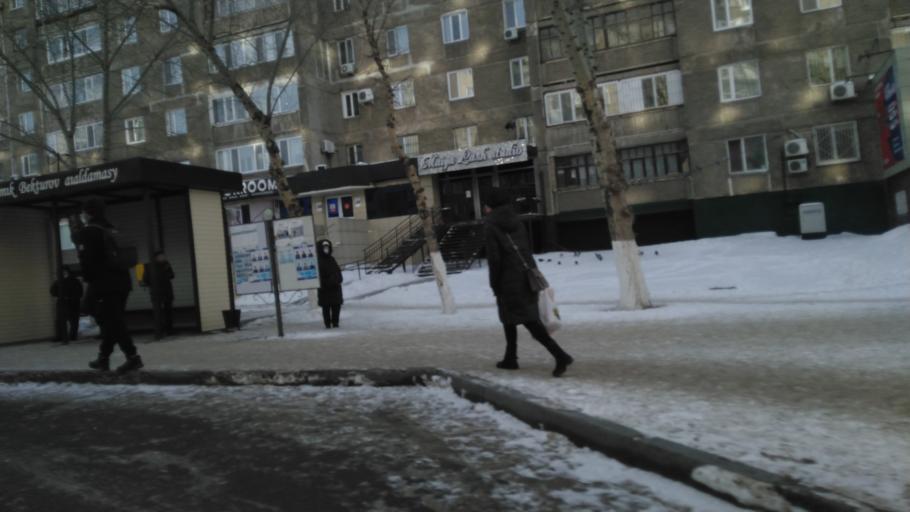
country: KZ
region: Pavlodar
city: Pavlodar
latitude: 52.2676
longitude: 76.9505
